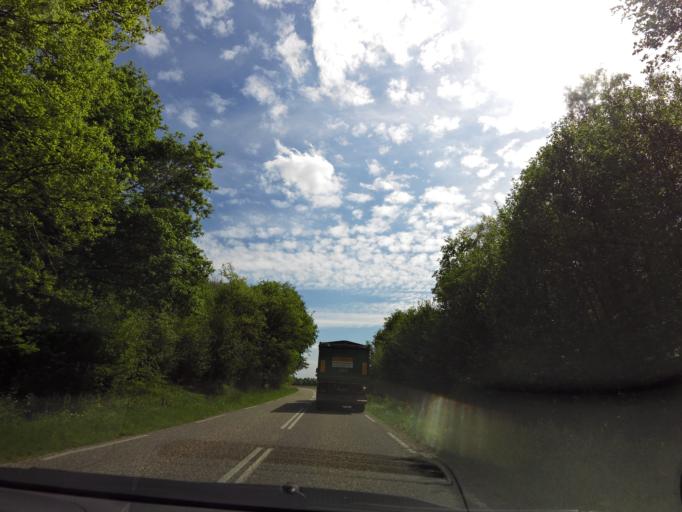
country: NL
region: Limburg
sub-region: Gemeente Leudal
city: Haelen
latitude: 51.2753
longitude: 5.9788
